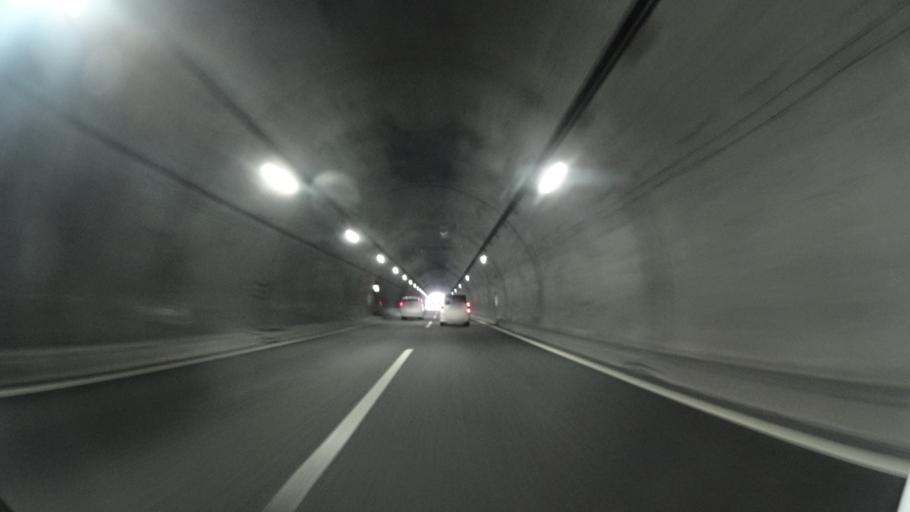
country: JP
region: Ehime
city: Saijo
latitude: 33.8861
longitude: 133.1614
